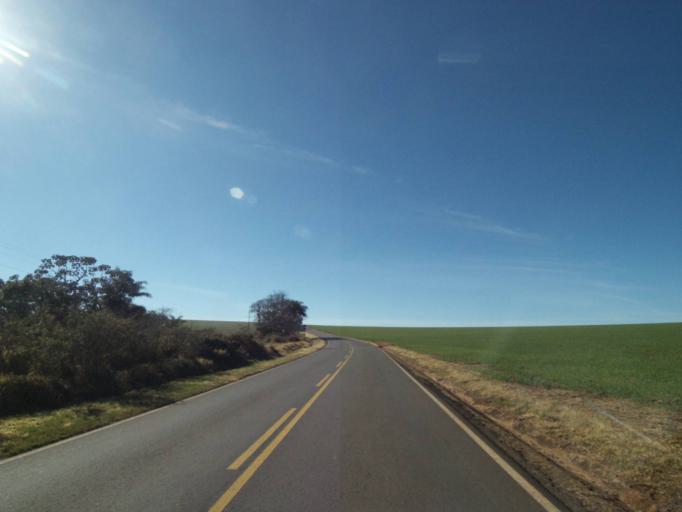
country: BR
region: Parana
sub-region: Tibagi
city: Tibagi
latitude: -24.5202
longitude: -50.3413
